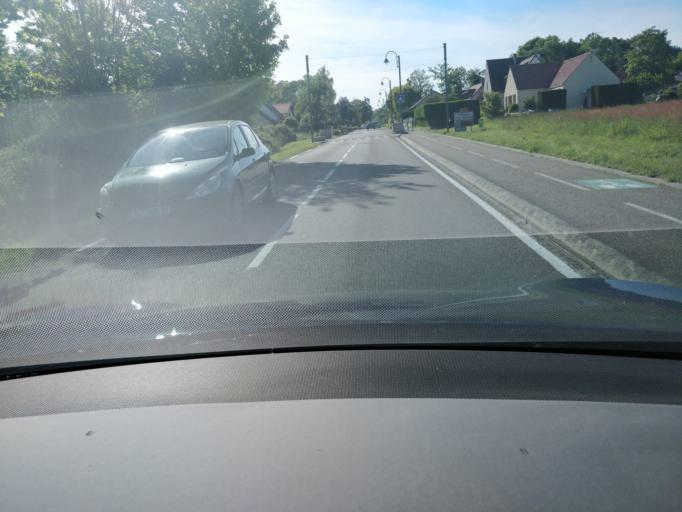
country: FR
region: Ile-de-France
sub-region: Departement de l'Essonne
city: Forges-les-Bains
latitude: 48.6260
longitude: 2.1102
